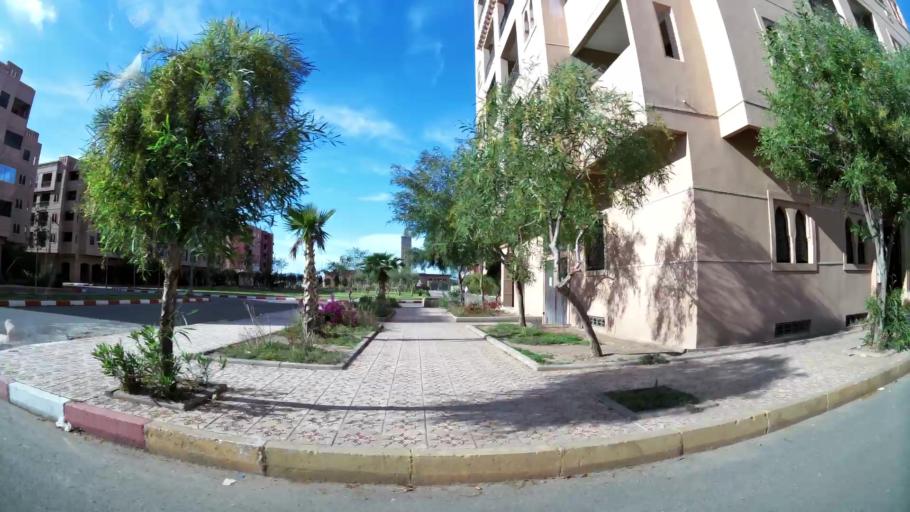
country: MA
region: Marrakech-Tensift-Al Haouz
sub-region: Marrakech
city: Marrakesh
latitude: 31.6882
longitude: -8.0687
